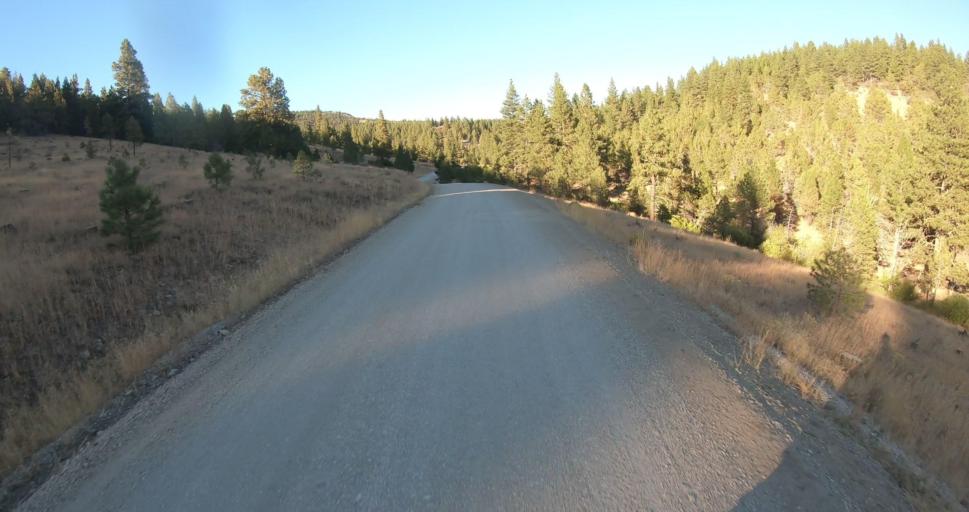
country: US
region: Oregon
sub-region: Lake County
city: Lakeview
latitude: 42.1956
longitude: -120.3068
